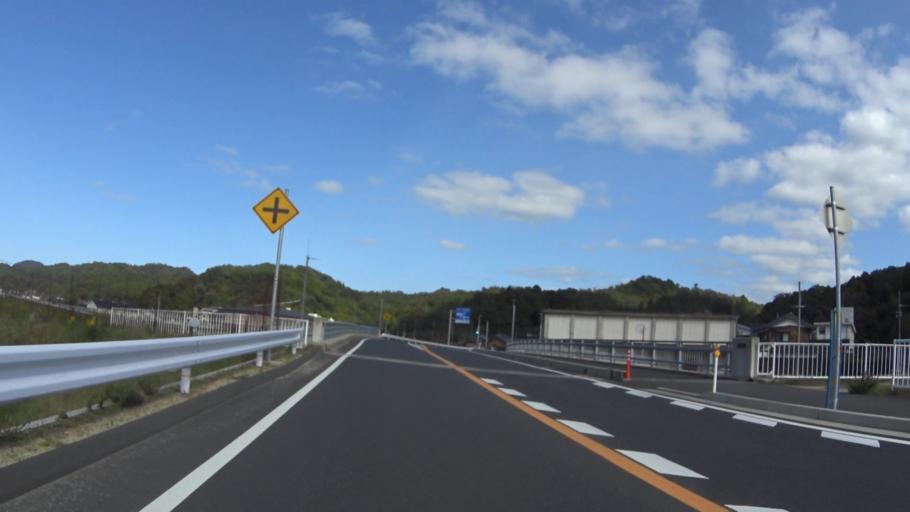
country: JP
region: Hyogo
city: Toyooka
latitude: 35.5896
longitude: 134.9298
